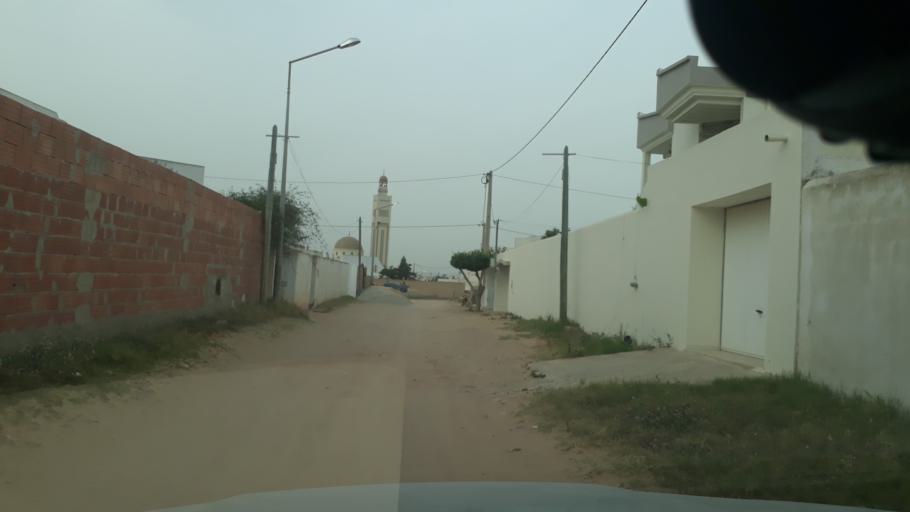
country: TN
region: Safaqis
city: Al Qarmadah
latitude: 34.7828
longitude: 10.7713
